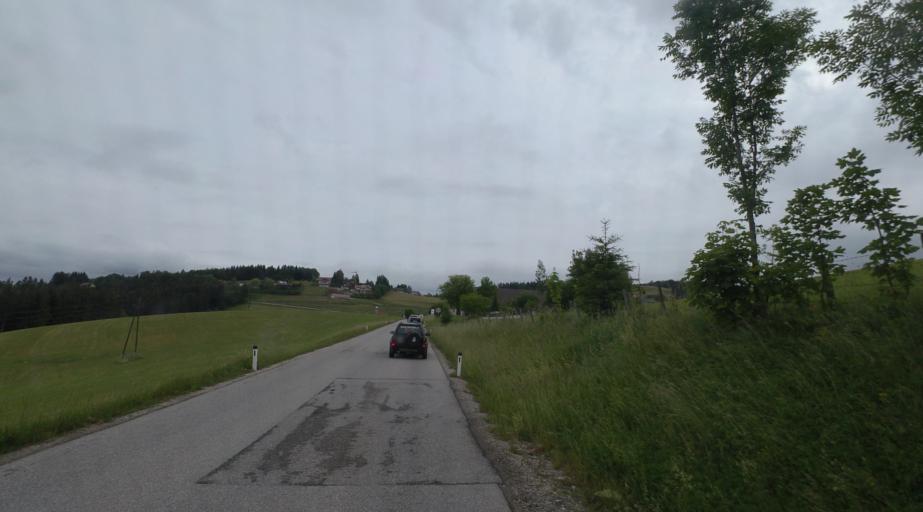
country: AT
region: Upper Austria
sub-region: Politischer Bezirk Kirchdorf an der Krems
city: Micheldorf in Oberoesterreich
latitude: 47.9294
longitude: 14.1740
